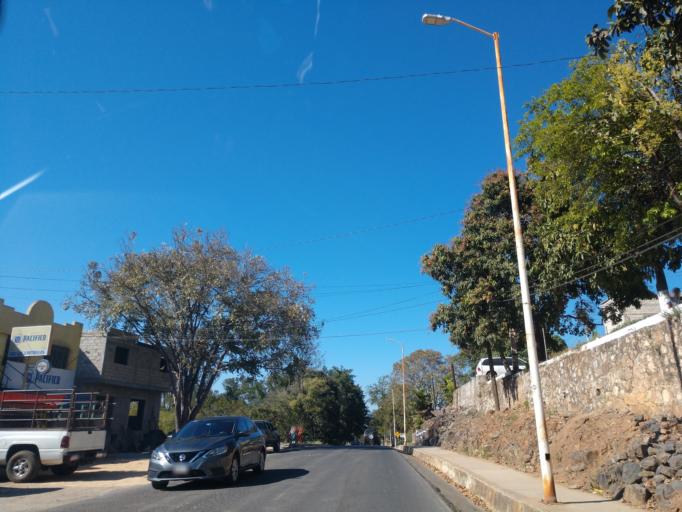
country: MX
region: Nayarit
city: Compostela
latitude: 21.2442
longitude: -104.9010
